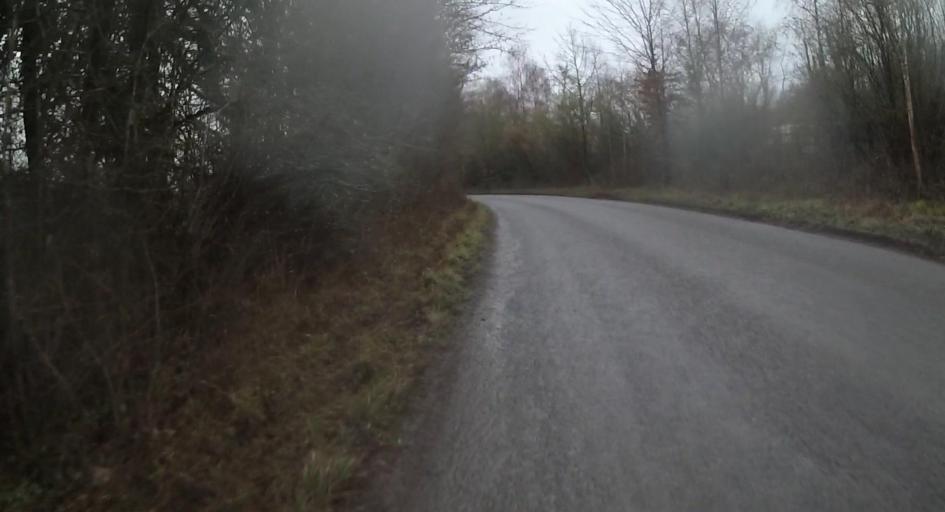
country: GB
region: England
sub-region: Hampshire
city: Four Marks
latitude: 51.0796
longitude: -1.1577
